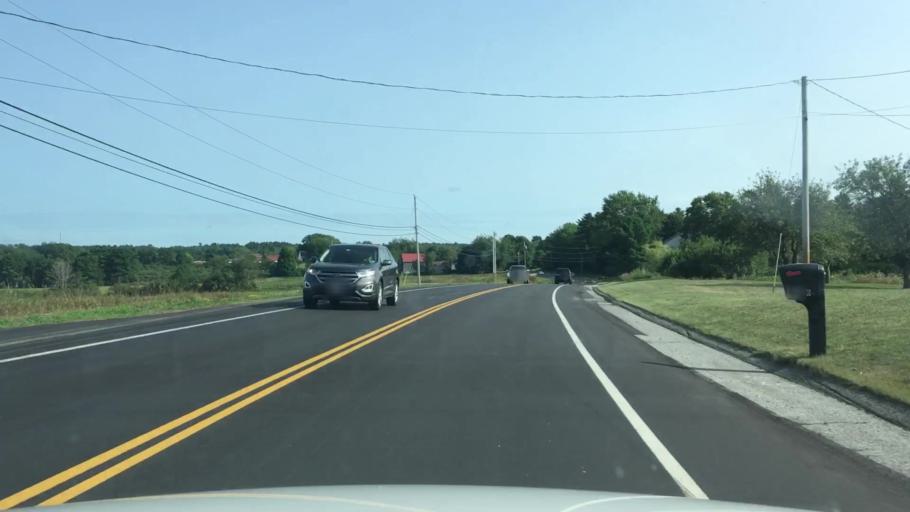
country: US
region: Maine
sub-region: Knox County
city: Warren
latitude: 44.1041
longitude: -69.2502
